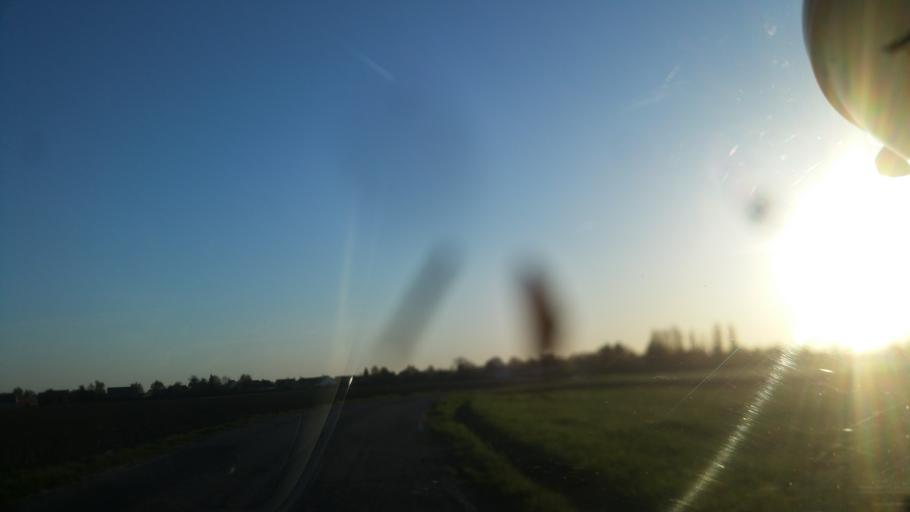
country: FR
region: Ile-de-France
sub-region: Departement de l'Essonne
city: Limours
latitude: 48.6365
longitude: 2.0655
